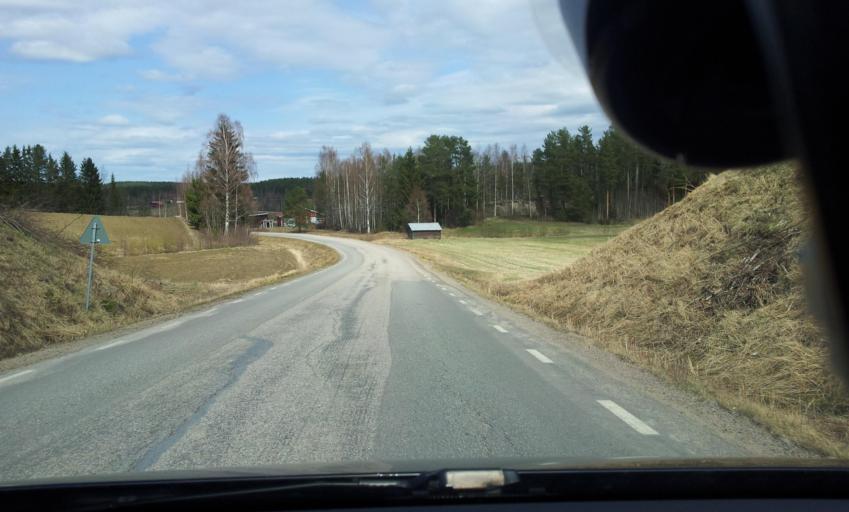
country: SE
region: Gaevleborg
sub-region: Ljusdals Kommun
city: Ljusdal
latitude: 61.7668
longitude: 16.0437
